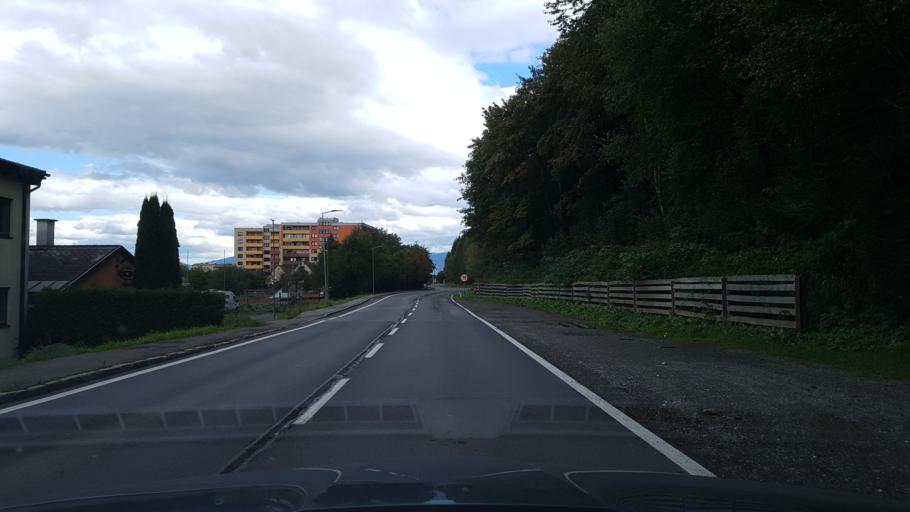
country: AT
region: Styria
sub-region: Politischer Bezirk Murtal
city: Judenburg
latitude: 47.1674
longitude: 14.6749
